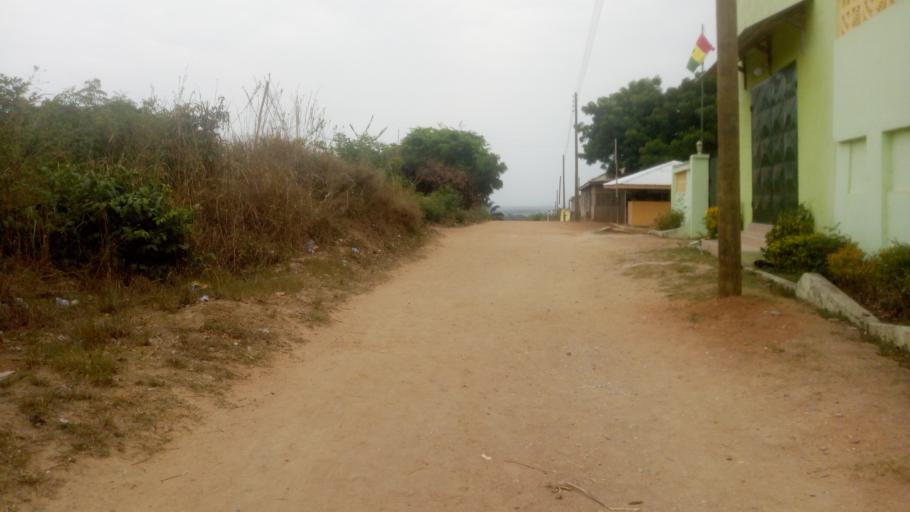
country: GH
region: Central
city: Winneba
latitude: 5.3598
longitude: -0.6263
